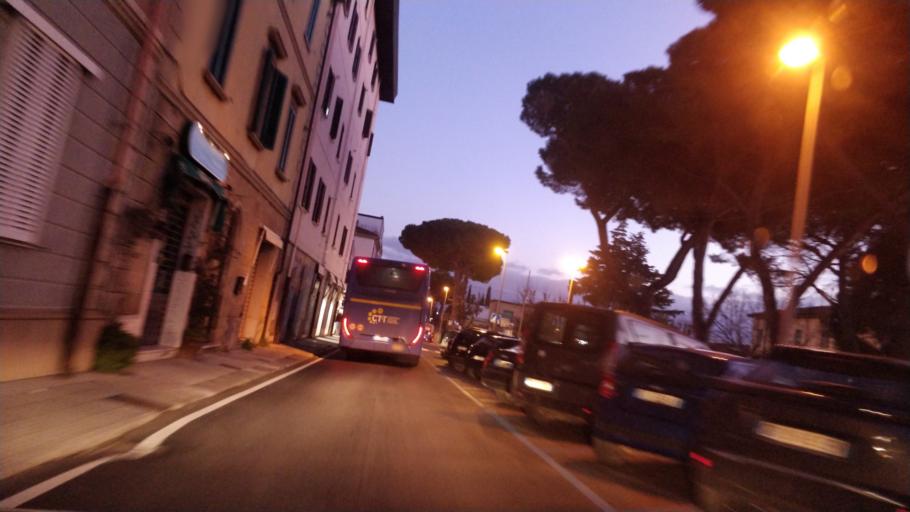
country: IT
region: Tuscany
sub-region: Provincia di Livorno
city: Cecina
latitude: 43.3113
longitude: 10.5146
